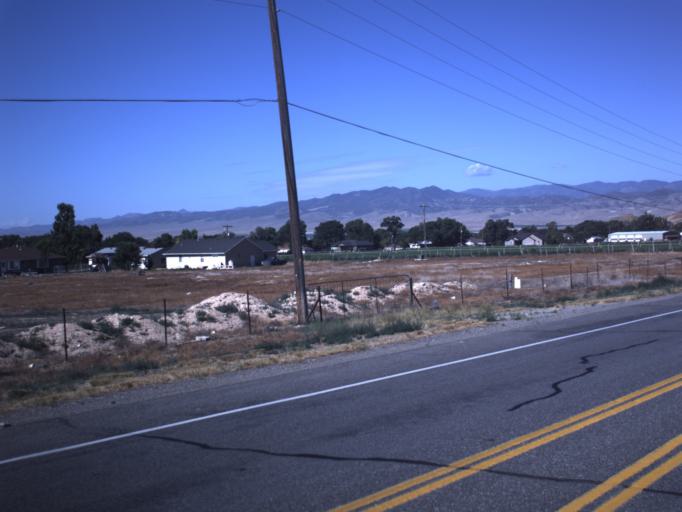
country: US
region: Utah
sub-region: Sanpete County
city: Gunnison
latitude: 39.1600
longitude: -111.8101
